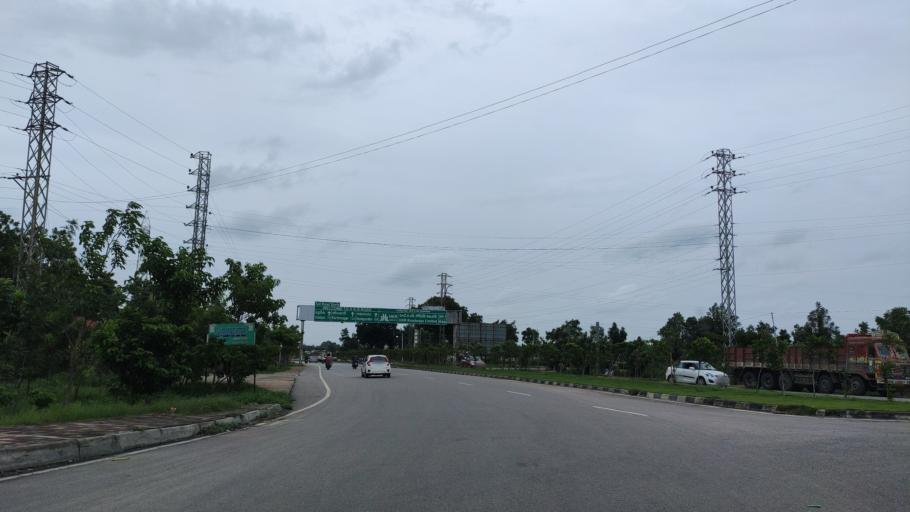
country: IN
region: Telangana
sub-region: Rangareddi
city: Secunderabad
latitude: 17.5798
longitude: 78.5744
